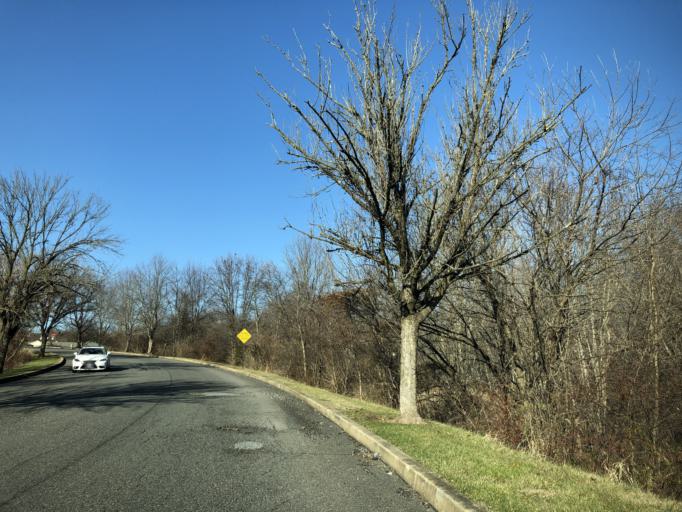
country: US
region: Pennsylvania
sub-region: Delaware County
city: Boothwyn
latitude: 39.8539
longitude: -75.4602
